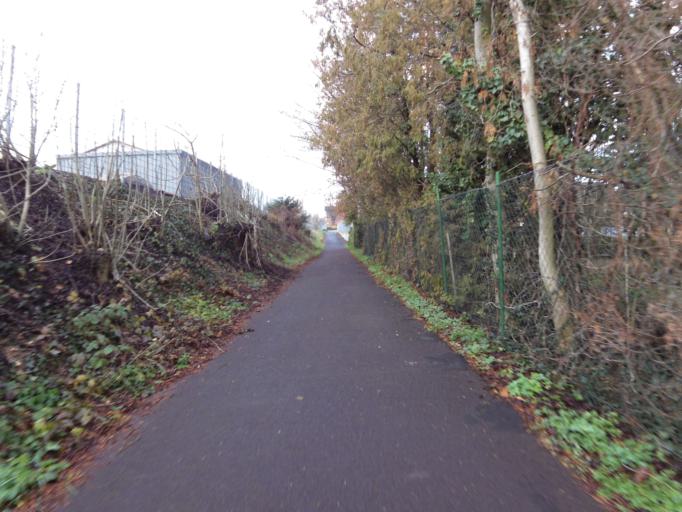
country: DE
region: Rheinland-Pfalz
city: Offstein
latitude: 49.6038
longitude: 8.2401
